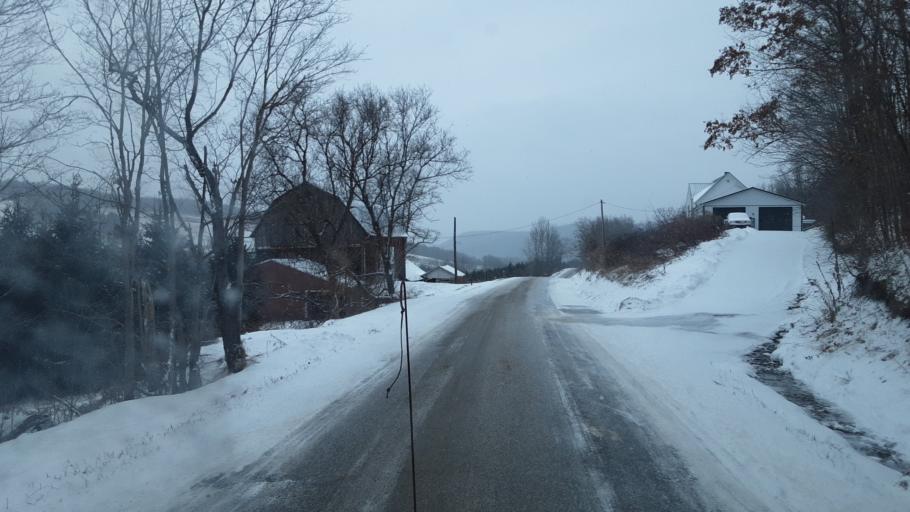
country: US
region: Pennsylvania
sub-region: Tioga County
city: Westfield
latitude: 41.9544
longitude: -77.6952
